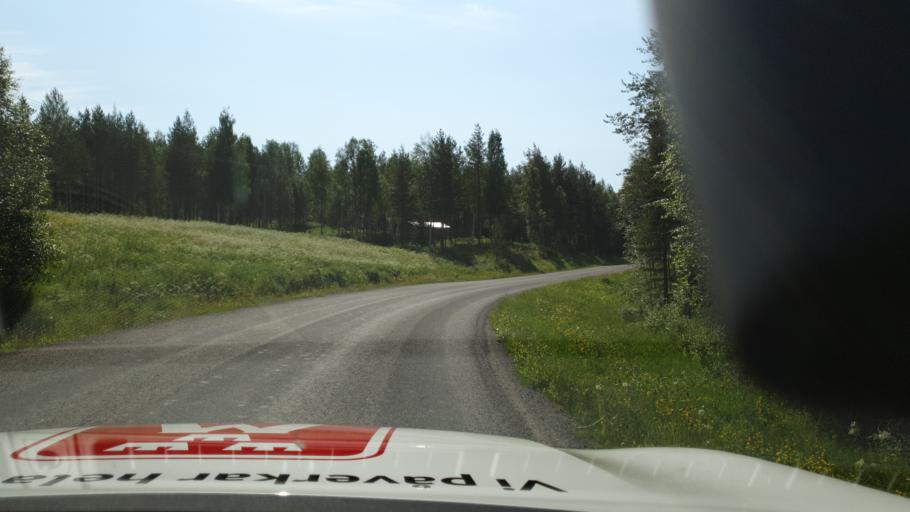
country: SE
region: Vaesterbotten
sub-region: Skelleftea Kommun
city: Langsele
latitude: 65.0098
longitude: 20.0880
